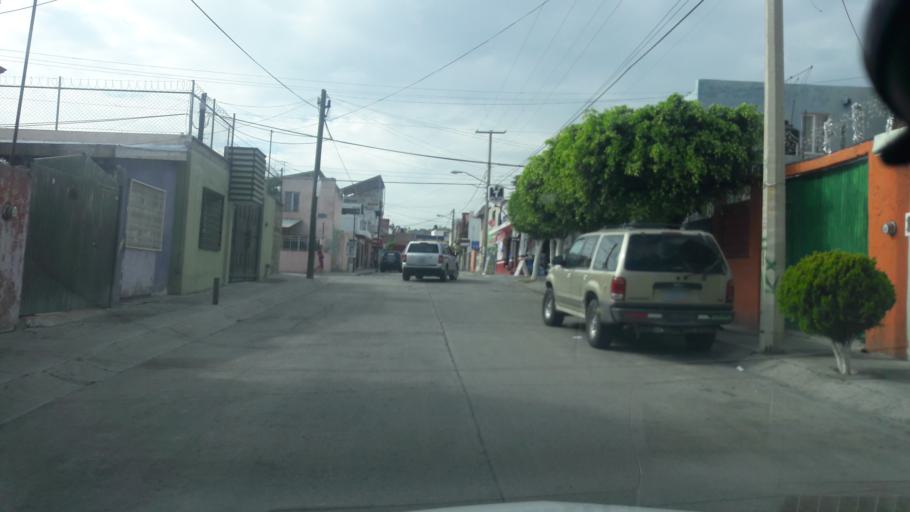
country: MX
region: Guanajuato
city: Leon
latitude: 21.1443
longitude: -101.7006
